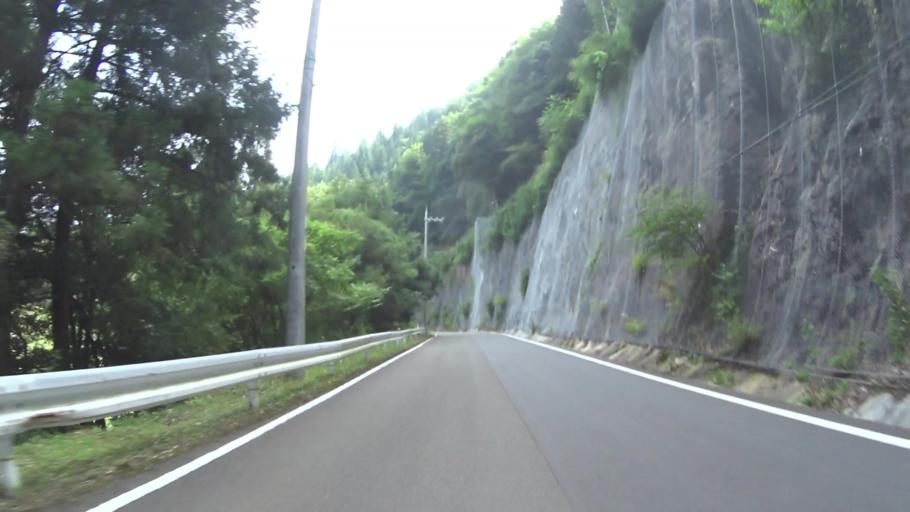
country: JP
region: Fukui
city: Obama
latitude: 35.3101
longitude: 135.6420
